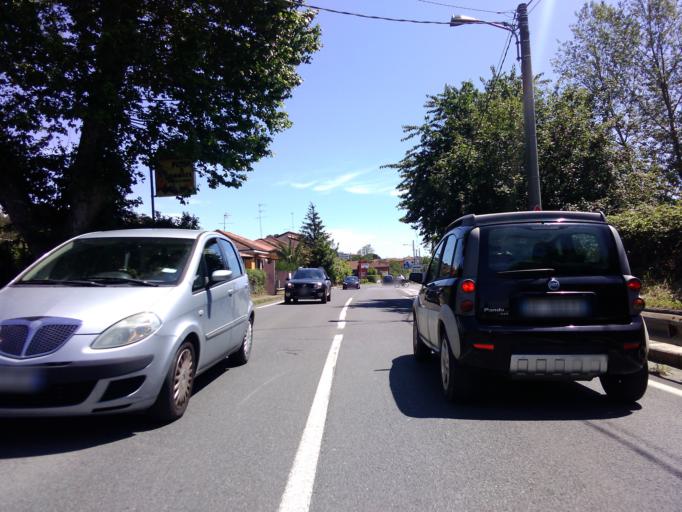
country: IT
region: Liguria
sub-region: Provincia di La Spezia
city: Santo Stefano di Magra
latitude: 44.1285
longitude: 9.9424
